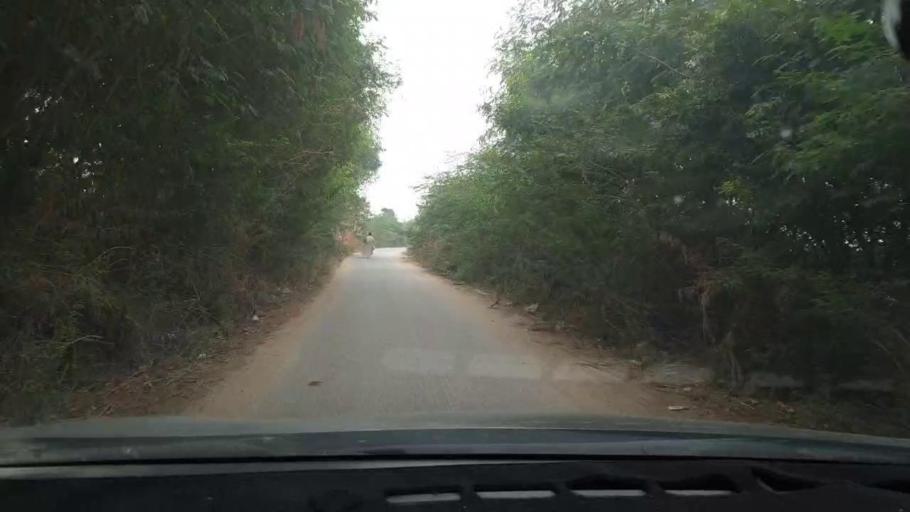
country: PK
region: Sindh
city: Malir Cantonment
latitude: 24.9243
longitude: 67.3202
